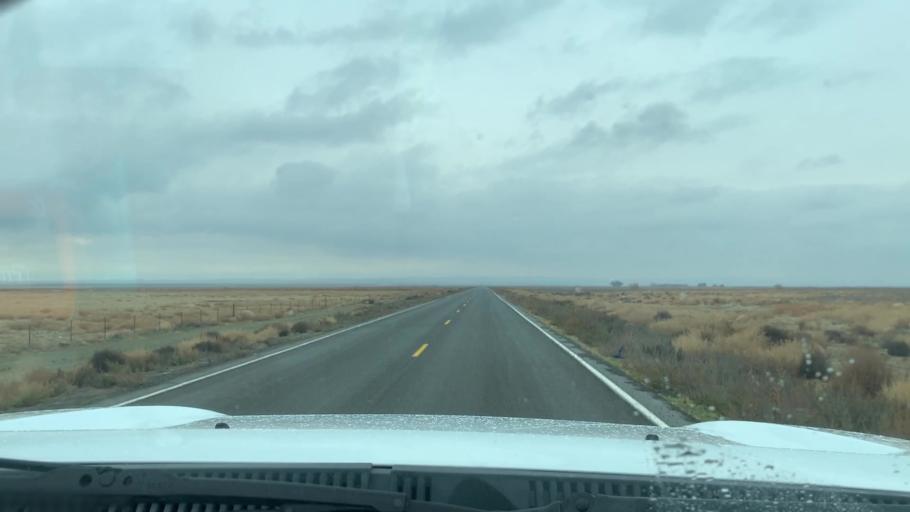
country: US
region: California
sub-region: Kings County
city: Kettleman City
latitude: 35.9341
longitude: -119.7858
